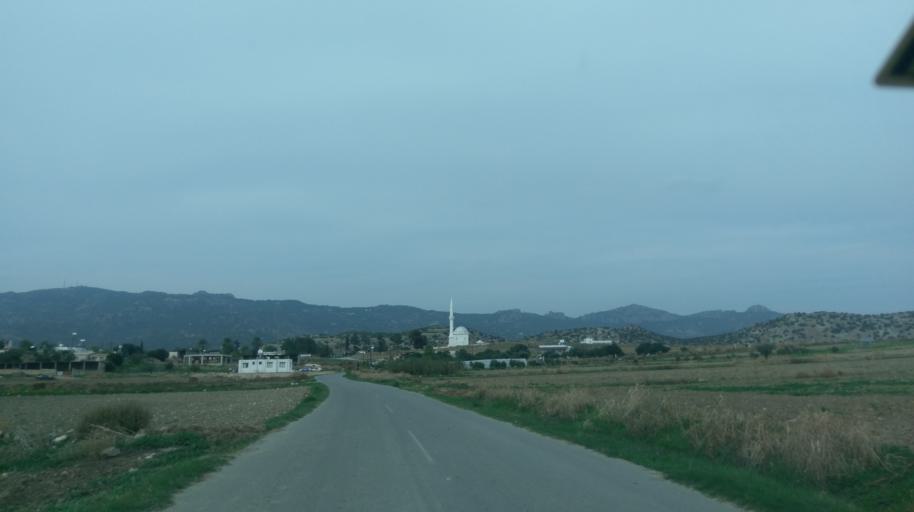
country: CY
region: Ammochostos
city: Trikomo
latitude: 35.3570
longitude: 33.9261
